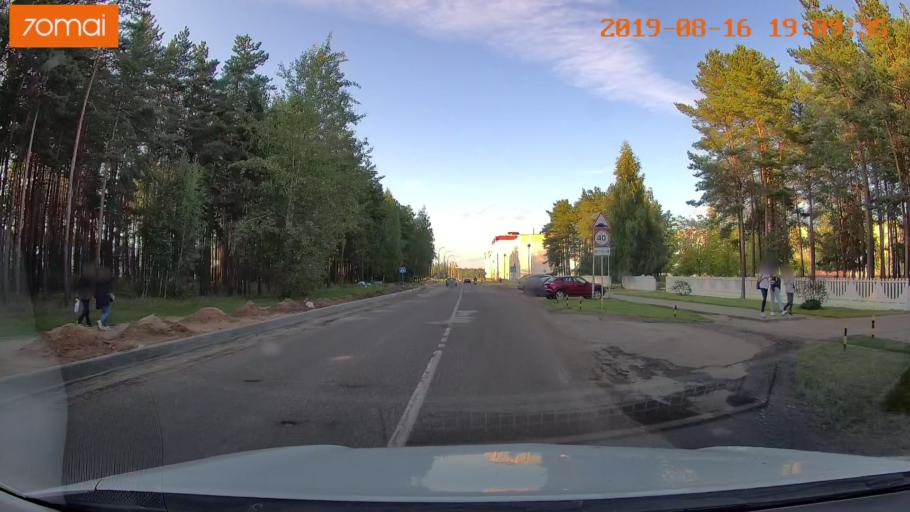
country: BY
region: Mogilev
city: Asipovichy
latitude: 53.3191
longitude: 28.6353
